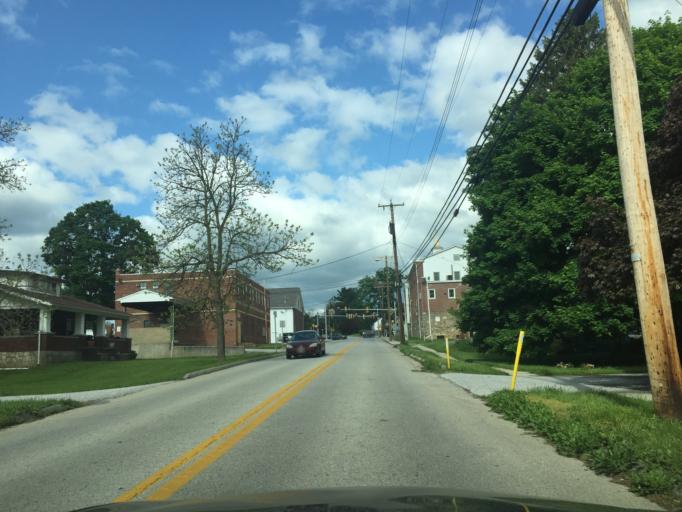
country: US
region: Maryland
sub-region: Baltimore County
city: Reisterstown
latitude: 39.4670
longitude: -76.8278
